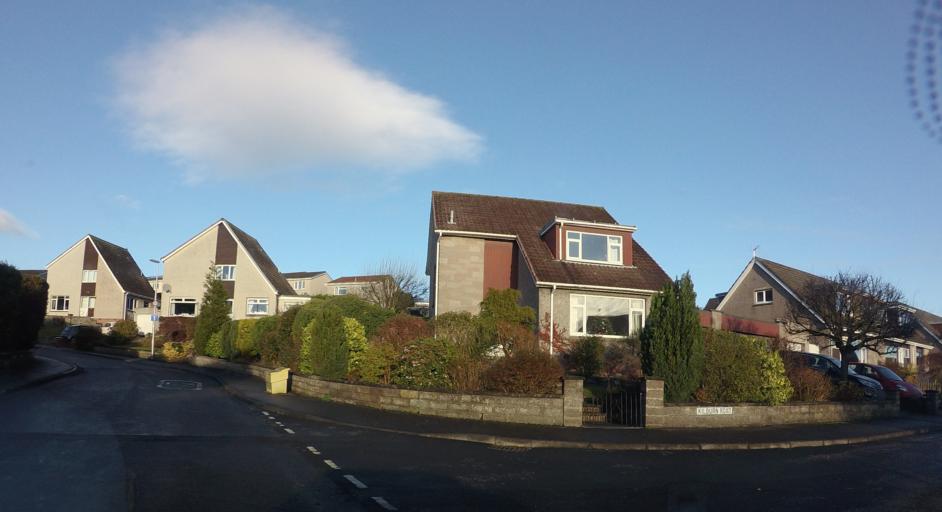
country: GB
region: Scotland
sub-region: Fife
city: Crossford
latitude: 56.0643
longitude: -3.5065
